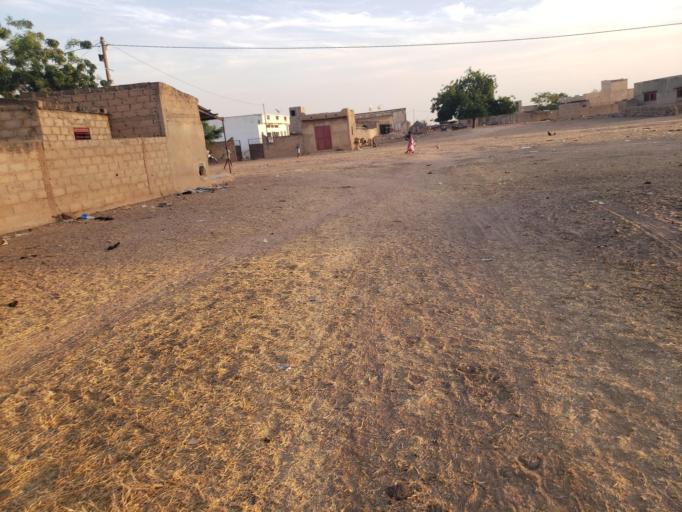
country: SN
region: Matam
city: Ranerou
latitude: 15.2970
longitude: -13.9654
